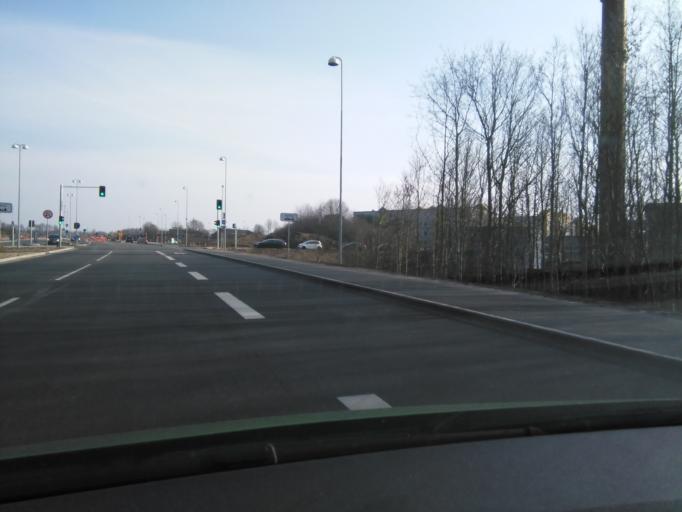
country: DK
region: Central Jutland
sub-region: Arhus Kommune
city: Arhus
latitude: 56.1840
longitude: 10.1670
